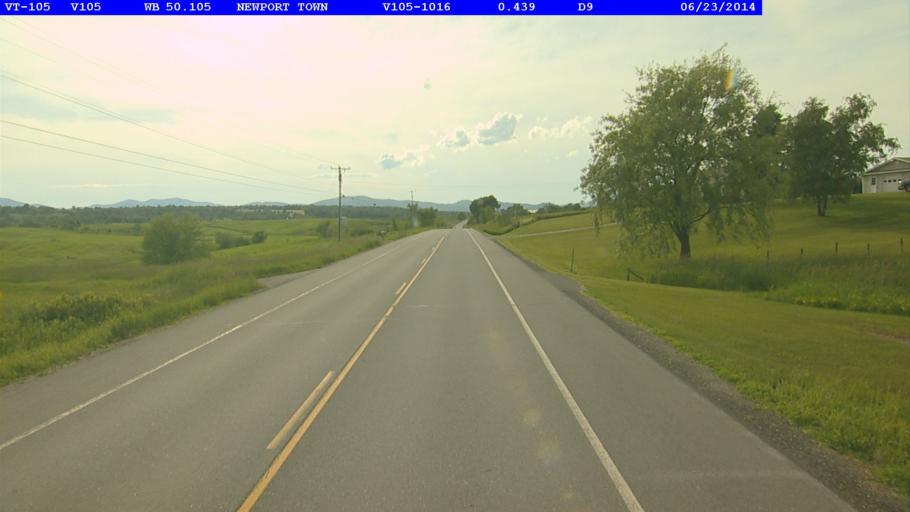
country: US
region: Vermont
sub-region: Orleans County
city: Newport
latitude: 44.9756
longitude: -72.3278
